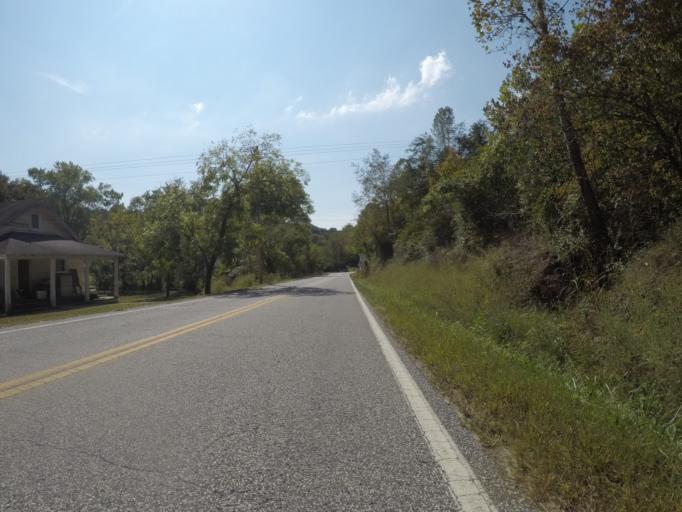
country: US
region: West Virginia
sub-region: Cabell County
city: Lesage
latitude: 38.5524
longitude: -82.3910
